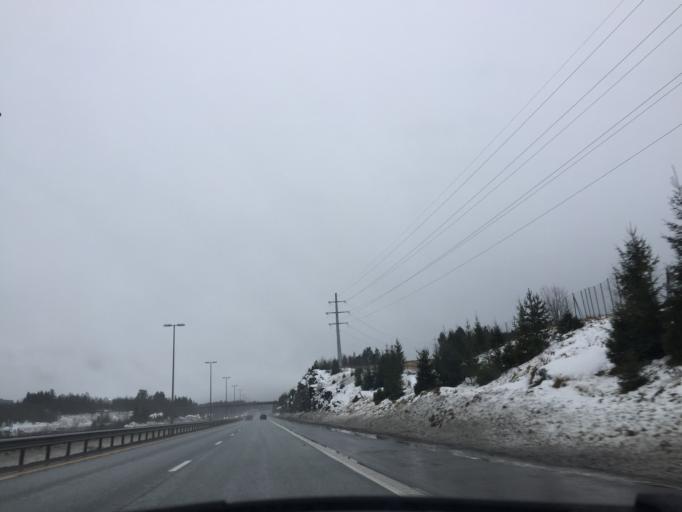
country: NO
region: Akershus
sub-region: Vestby
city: Vestby
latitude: 59.5886
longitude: 10.7362
